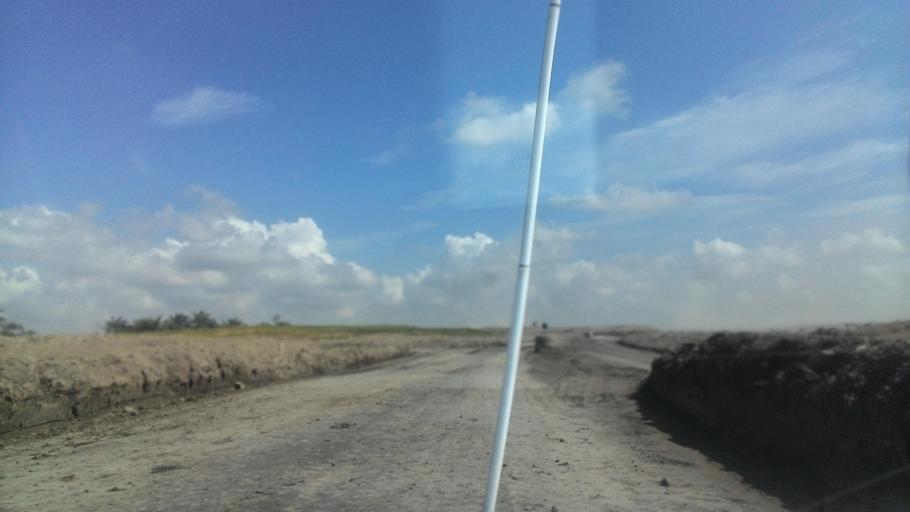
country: ID
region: South Kalimantan
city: Tanta
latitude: -2.1864
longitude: 115.4731
